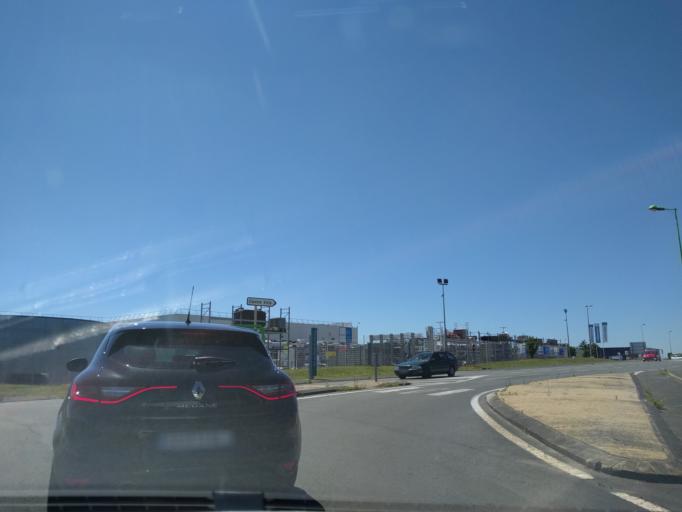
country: FR
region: Poitou-Charentes
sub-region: Departement des Deux-Sevres
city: Chauray
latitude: 46.3344
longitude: -0.4064
